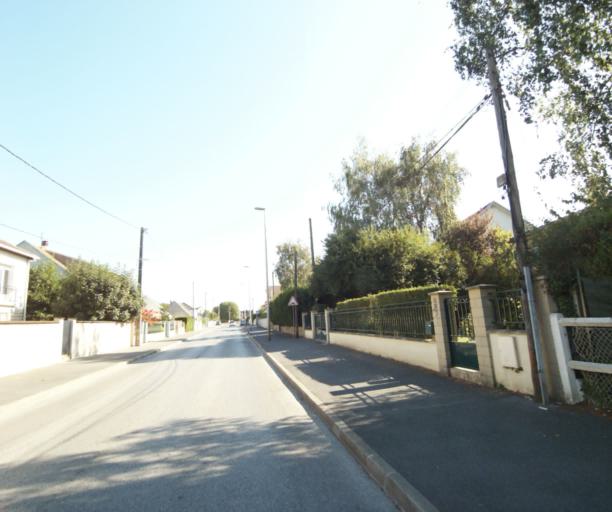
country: FR
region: Ile-de-France
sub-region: Departement de Seine-et-Marne
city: Lagny-sur-Marne
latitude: 48.8648
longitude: 2.7183
